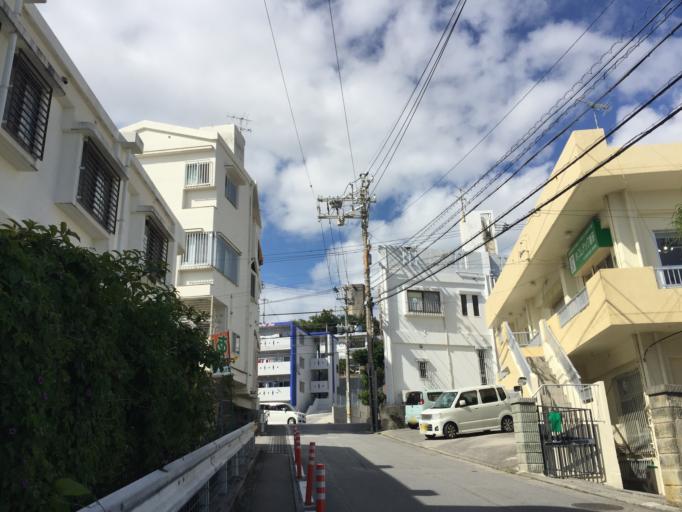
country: JP
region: Okinawa
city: Ginowan
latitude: 26.2360
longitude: 127.7327
